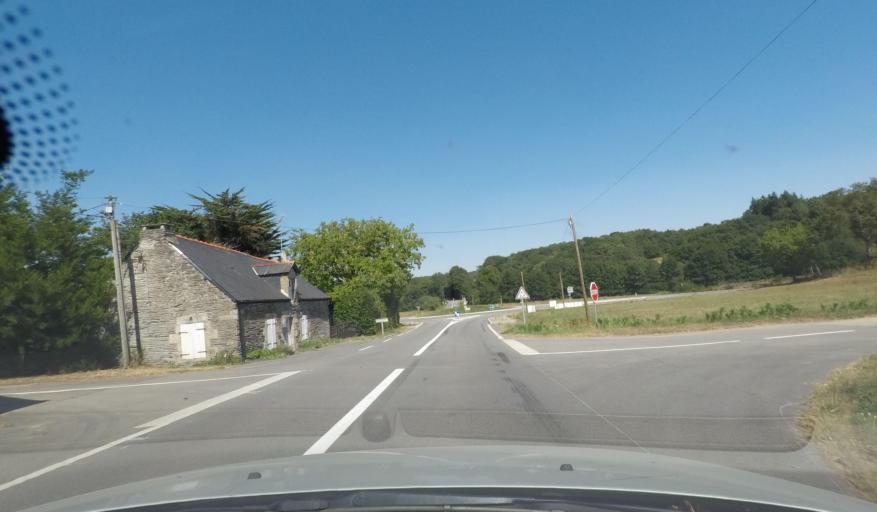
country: FR
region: Brittany
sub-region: Departement du Morbihan
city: Caro
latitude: 47.8371
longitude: -2.3120
